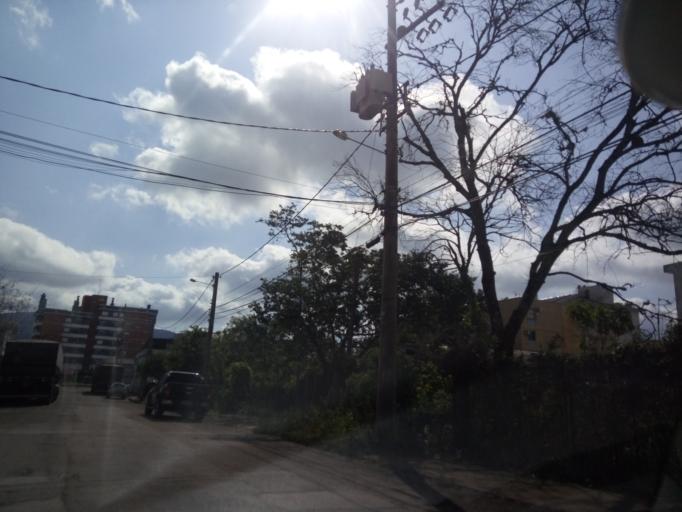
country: BR
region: Rio Grande do Sul
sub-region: Santa Maria
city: Santa Maria
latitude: -29.7027
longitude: -53.7196
